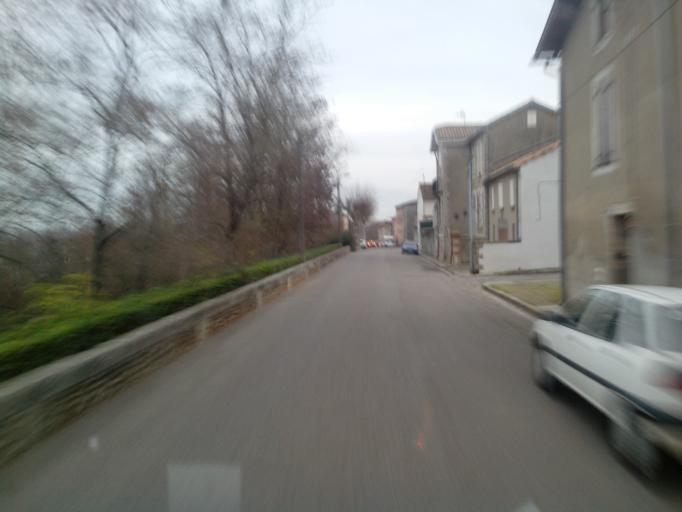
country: FR
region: Midi-Pyrenees
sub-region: Departement de l'Ariege
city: Mazeres
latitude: 43.2538
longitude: 1.6778
